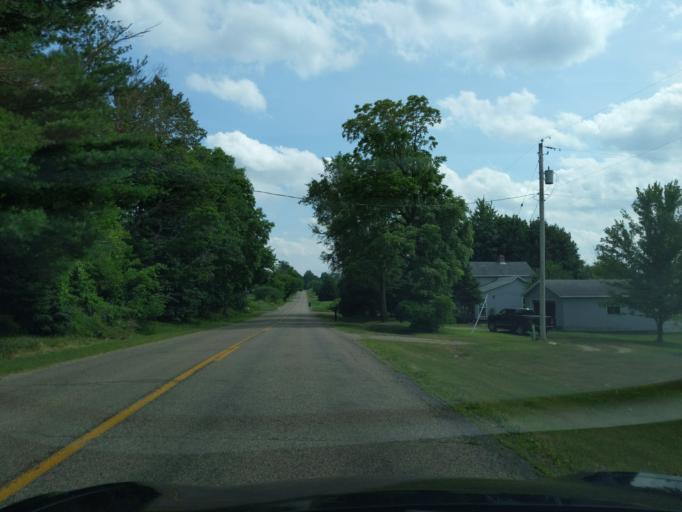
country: US
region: Michigan
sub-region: Eaton County
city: Eaton Rapids
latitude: 42.5395
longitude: -84.6018
